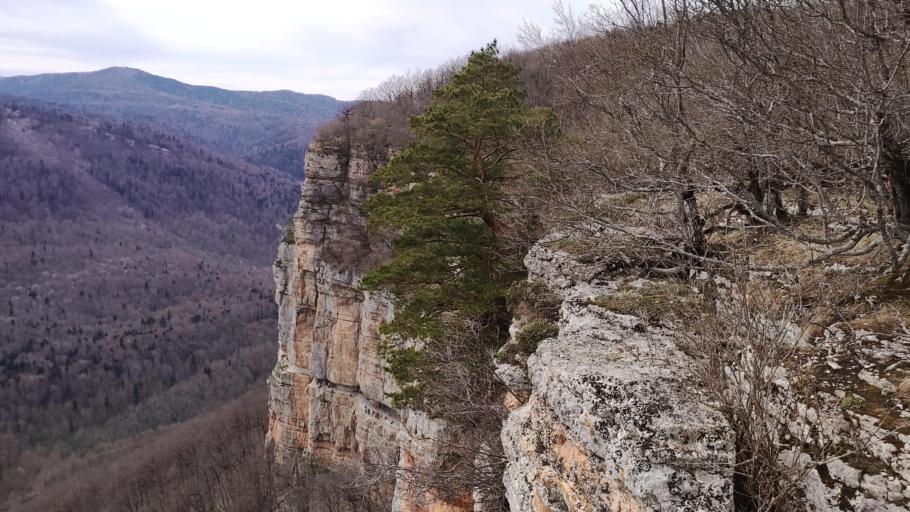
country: RU
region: Adygeya
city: Kamennomostskiy
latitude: 44.2102
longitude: 39.9379
